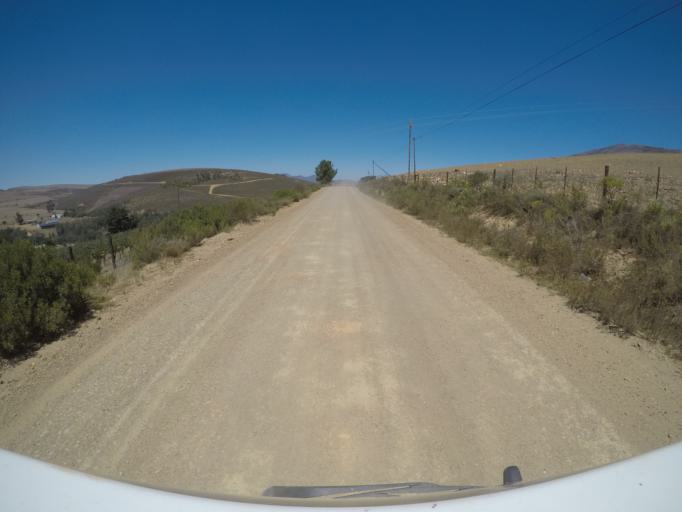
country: ZA
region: Western Cape
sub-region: Overberg District Municipality
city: Caledon
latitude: -34.1760
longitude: 19.2258
